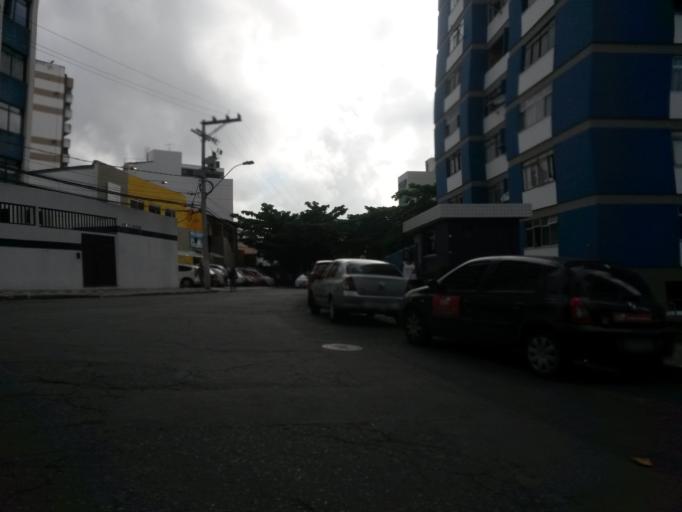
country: BR
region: Bahia
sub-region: Salvador
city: Salvador
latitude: -13.0015
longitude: -38.4616
